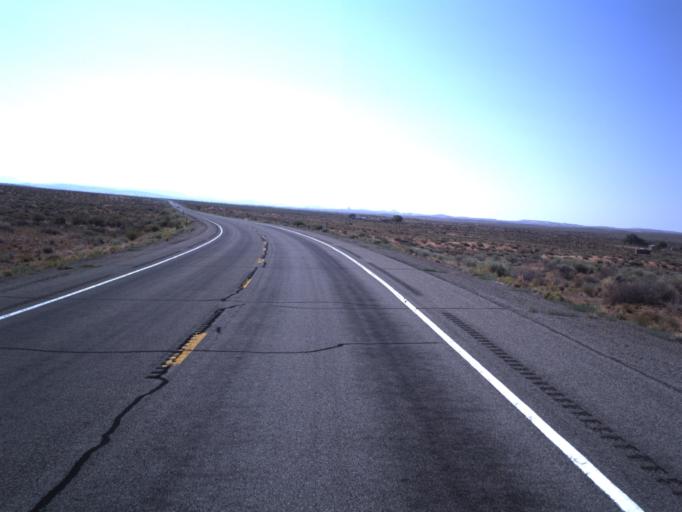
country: US
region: Utah
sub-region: San Juan County
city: Blanding
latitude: 37.2234
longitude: -109.6174
